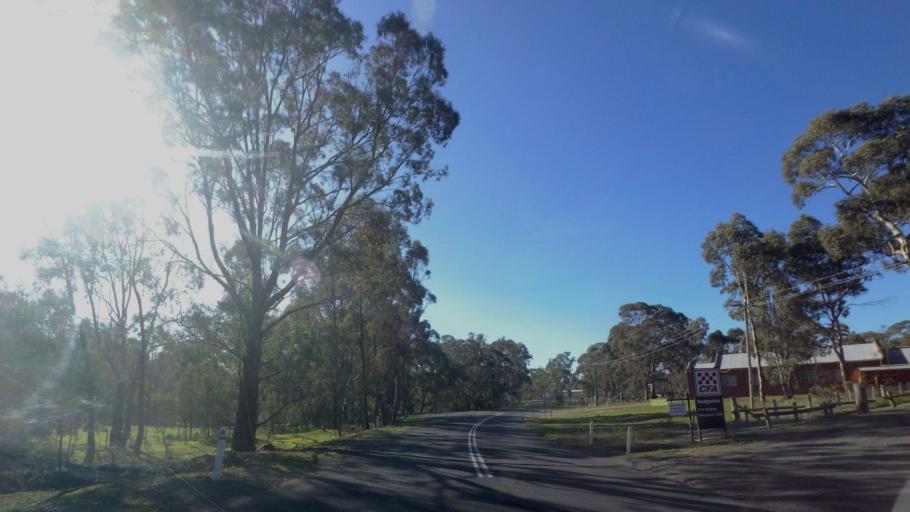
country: AU
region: Victoria
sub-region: Greater Bendigo
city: Kennington
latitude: -36.8718
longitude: 144.3151
